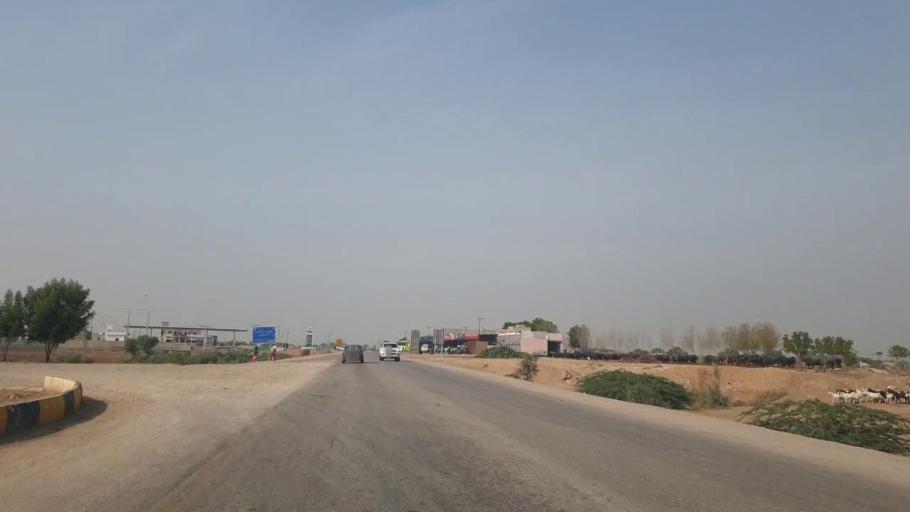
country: PK
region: Sindh
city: Sann
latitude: 26.1584
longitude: 68.0222
